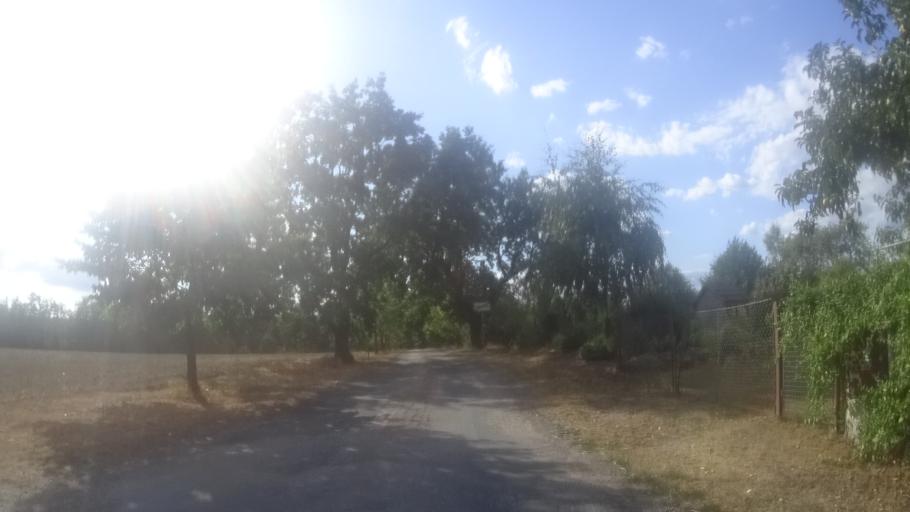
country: CZ
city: Albrechtice nad Orlici
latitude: 50.1566
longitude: 16.0438
